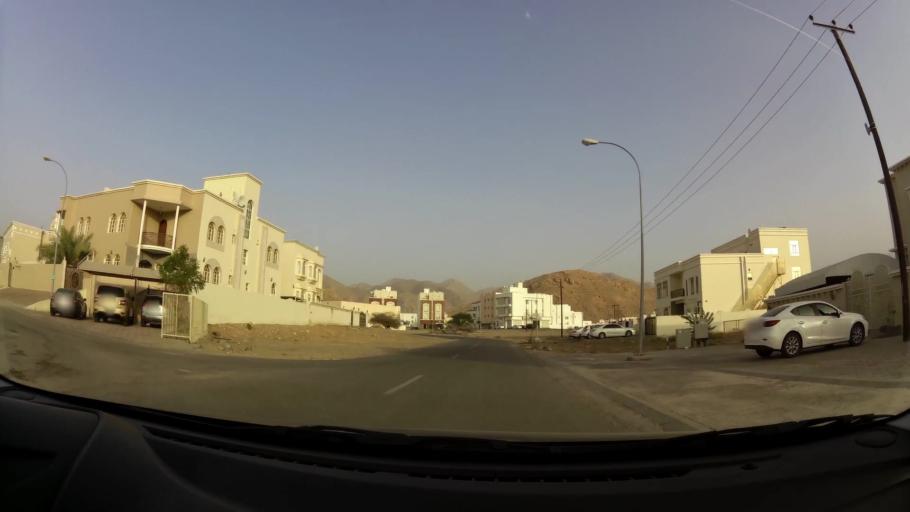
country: OM
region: Muhafazat Masqat
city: Bawshar
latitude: 23.5114
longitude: 58.3448
